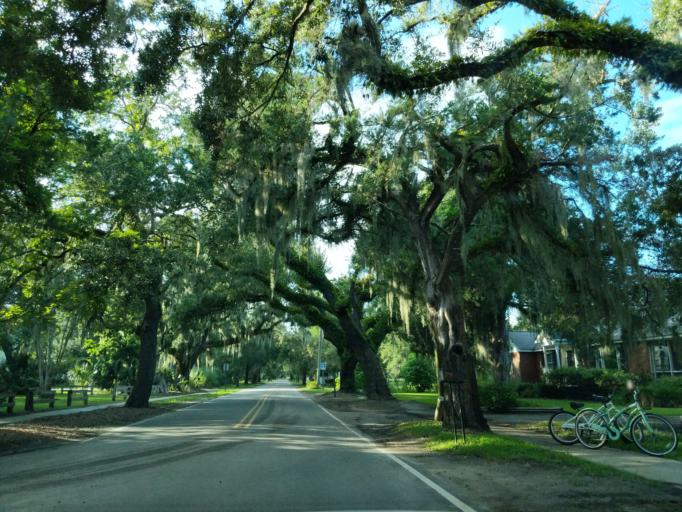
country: US
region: South Carolina
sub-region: Charleston County
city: Awendaw
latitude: 33.0813
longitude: -79.4586
